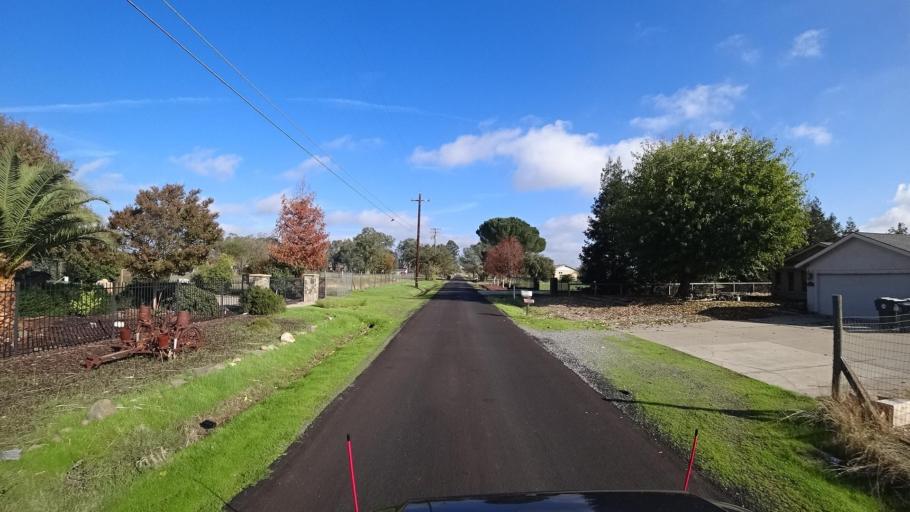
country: US
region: California
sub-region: Sacramento County
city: Elk Grove
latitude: 38.4290
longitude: -121.3655
